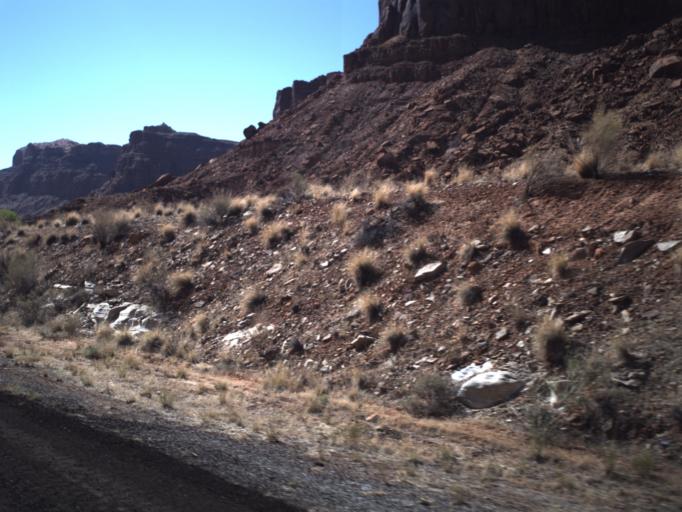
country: US
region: Utah
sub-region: San Juan County
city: Blanding
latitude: 37.9332
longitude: -110.4669
